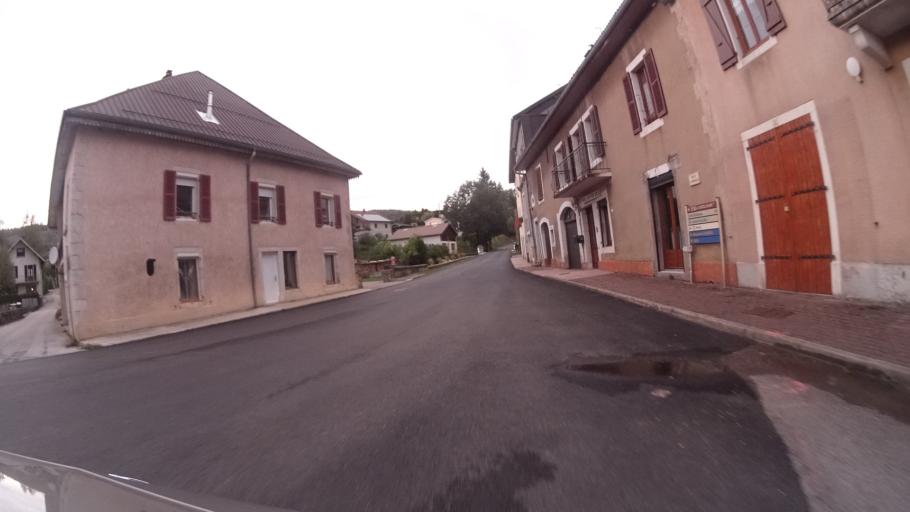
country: FR
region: Franche-Comte
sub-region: Departement du Jura
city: Morbier
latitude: 46.6598
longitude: 6.0755
